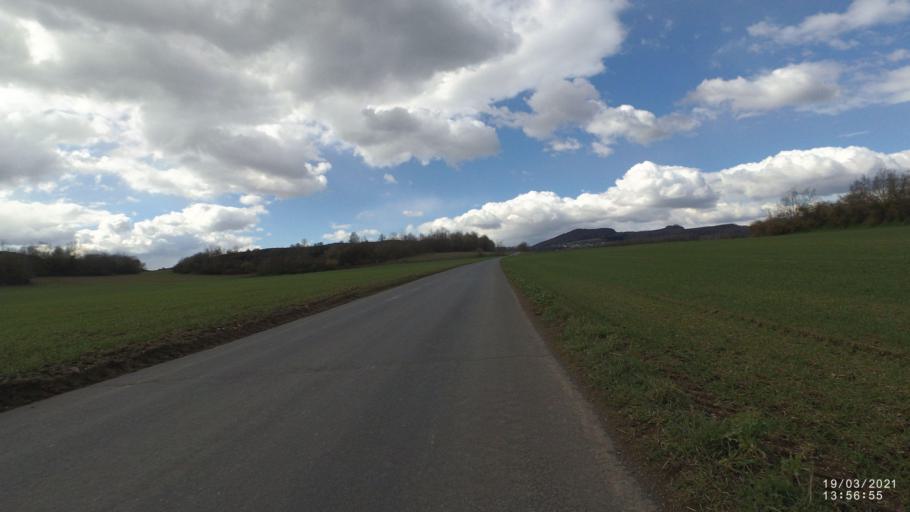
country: DE
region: Rheinland-Pfalz
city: Kretz
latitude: 50.4038
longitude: 7.3476
